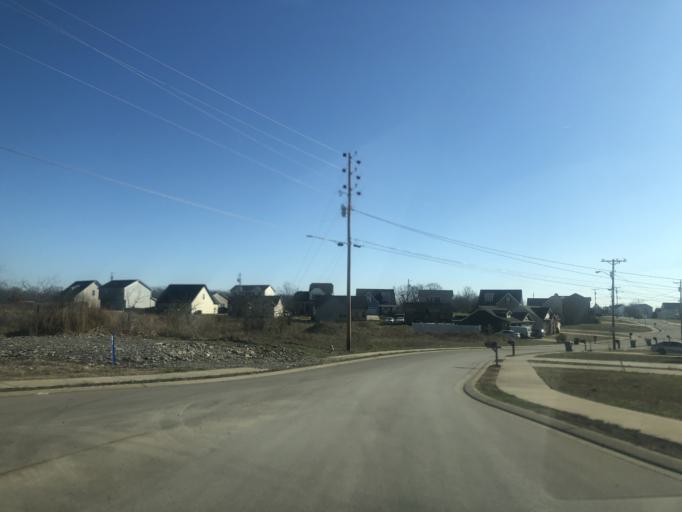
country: US
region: Tennessee
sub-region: Rutherford County
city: Smyrna
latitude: 35.9595
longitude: -86.5421
